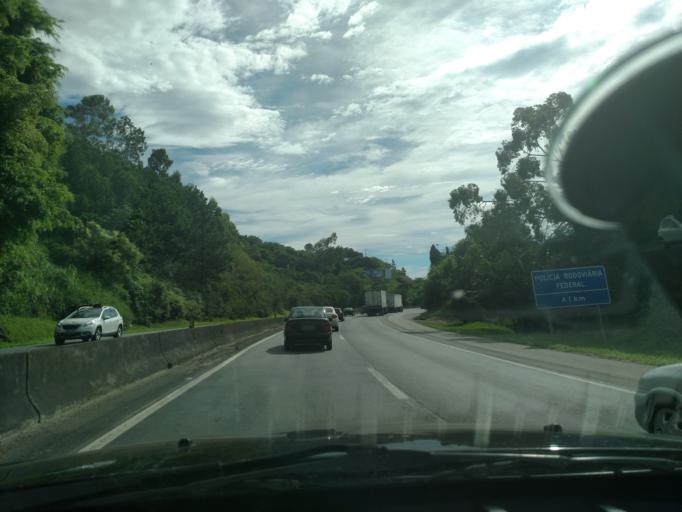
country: BR
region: Santa Catarina
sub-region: Biguacu
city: Biguacu
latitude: -27.4794
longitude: -48.6445
